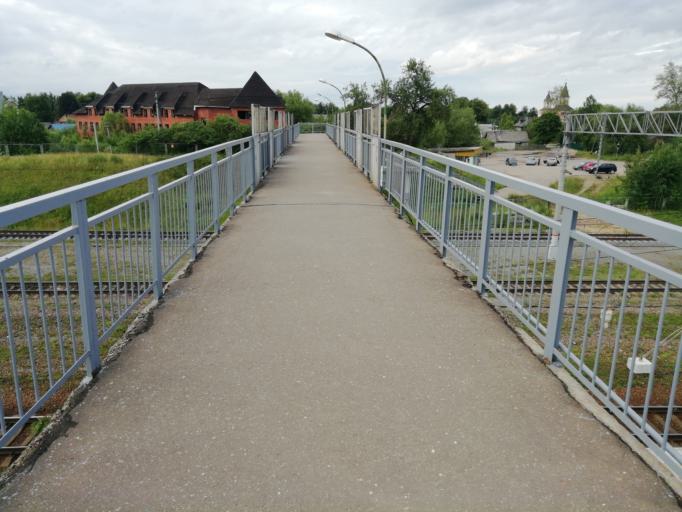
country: RU
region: Tverskaya
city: Spirovo
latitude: 57.4220
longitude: 34.9946
